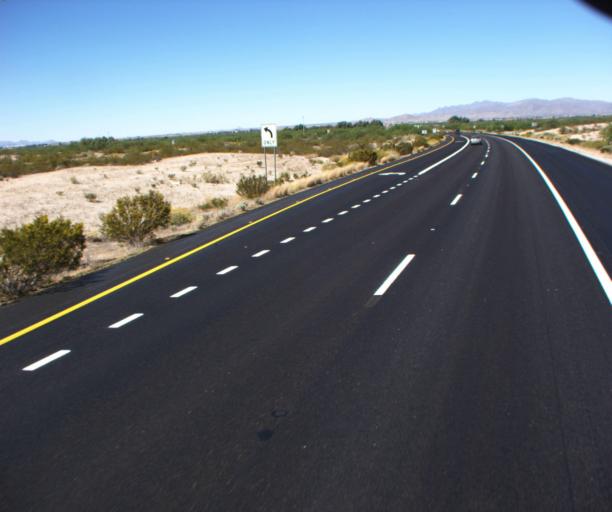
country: US
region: Arizona
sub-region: Maricopa County
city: Buckeye
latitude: 33.3161
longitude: -112.6232
